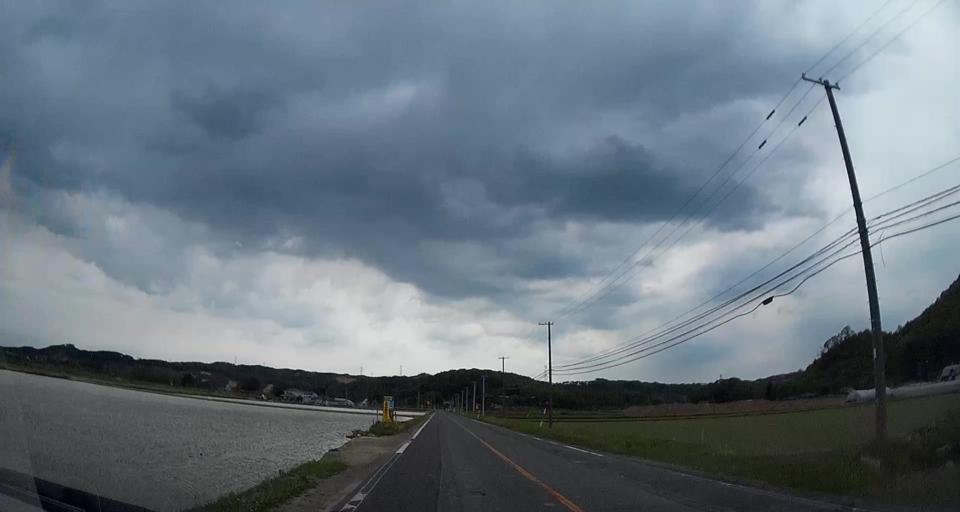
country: JP
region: Hokkaido
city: Chitose
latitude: 42.7559
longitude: 141.9346
